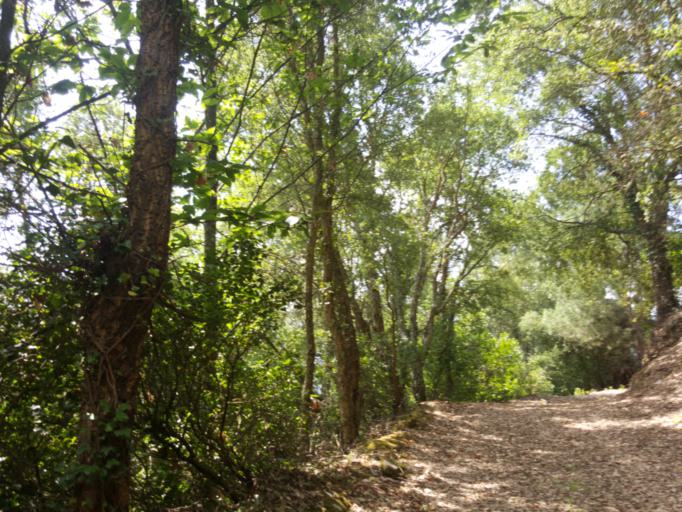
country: PT
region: Vila Real
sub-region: Mesao Frio
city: Mesao Frio
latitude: 41.1724
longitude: -7.8425
